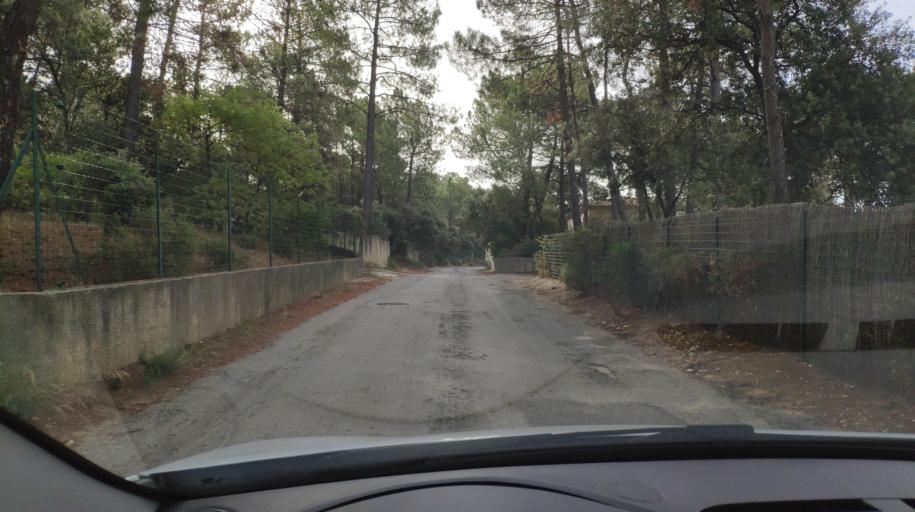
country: FR
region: Provence-Alpes-Cote d'Azur
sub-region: Departement du Vaucluse
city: Bedoin
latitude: 44.1185
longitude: 5.1830
